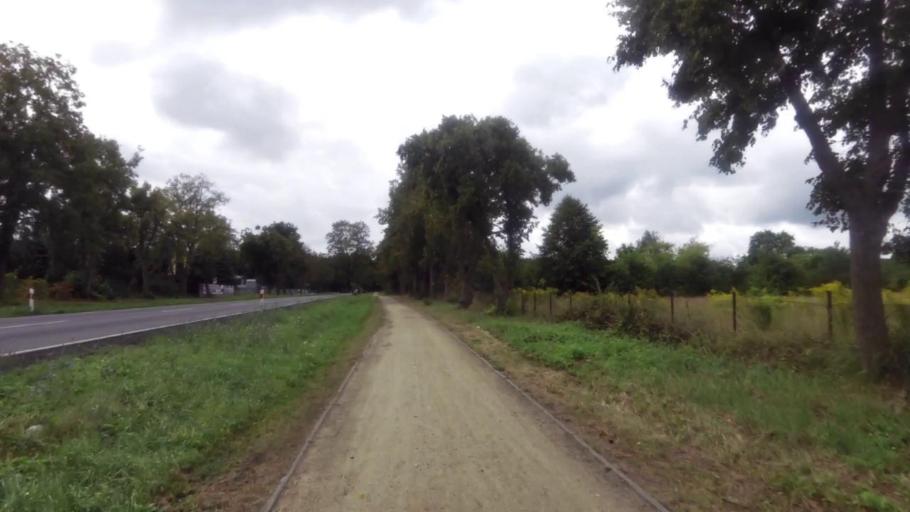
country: PL
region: West Pomeranian Voivodeship
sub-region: Powiat mysliborski
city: Debno
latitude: 52.7247
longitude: 14.6936
